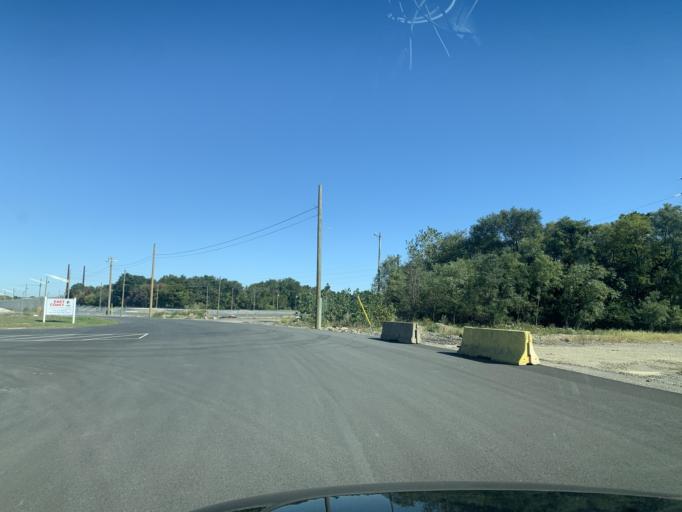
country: US
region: Maryland
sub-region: Baltimore County
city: Edgemere
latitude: 39.2327
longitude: -76.4819
